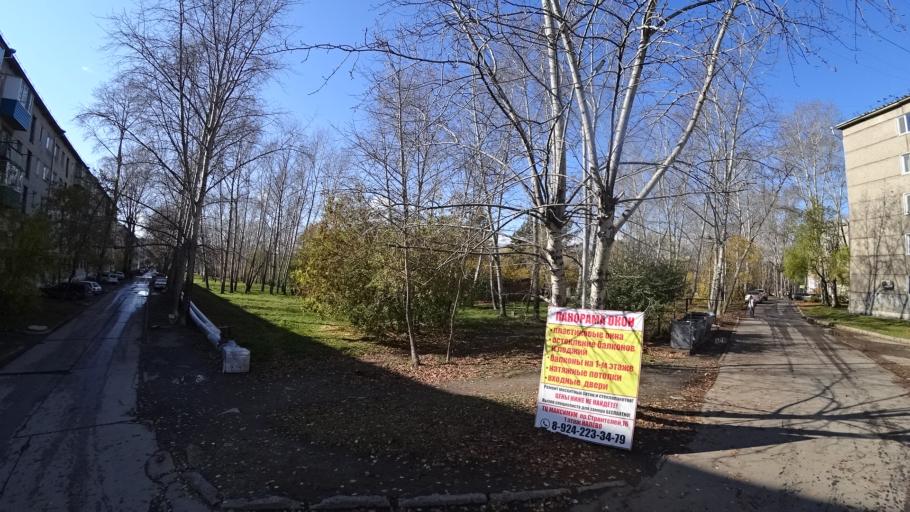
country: RU
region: Khabarovsk Krai
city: Amursk
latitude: 50.2259
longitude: 136.9077
